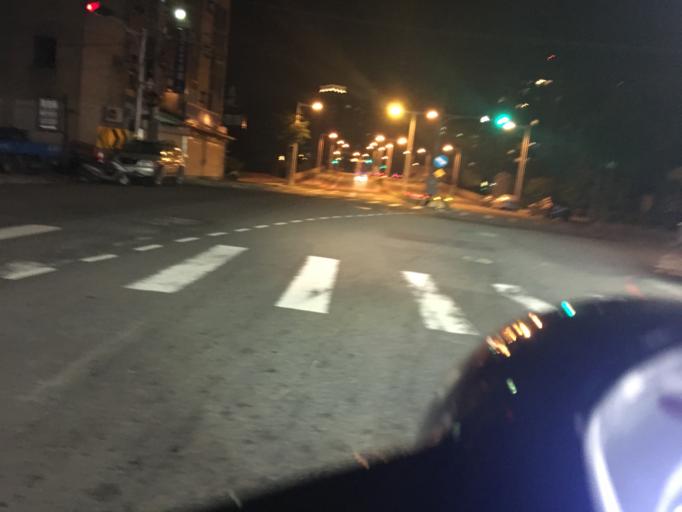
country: TW
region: Taiwan
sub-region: Hsinchu
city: Zhubei
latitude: 24.8333
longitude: 120.9982
